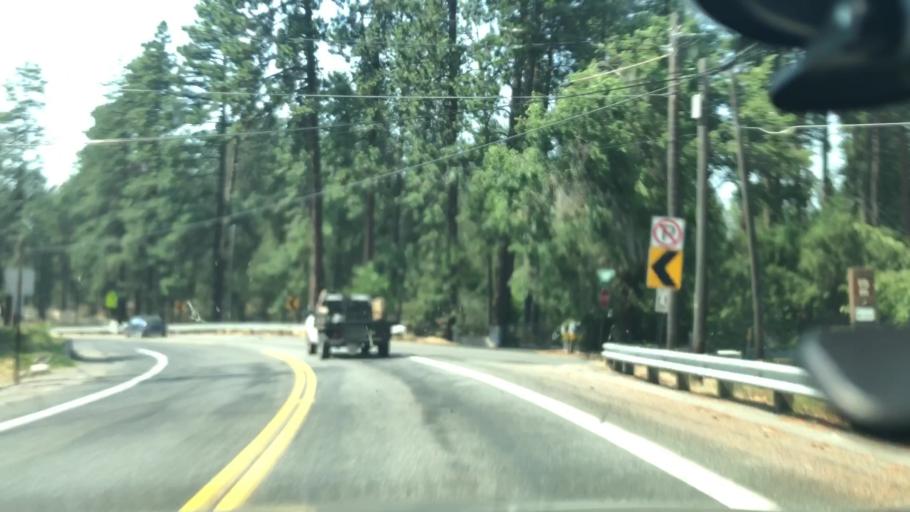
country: US
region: Washington
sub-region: Spokane County
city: Millwood
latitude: 47.6982
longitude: -117.2880
